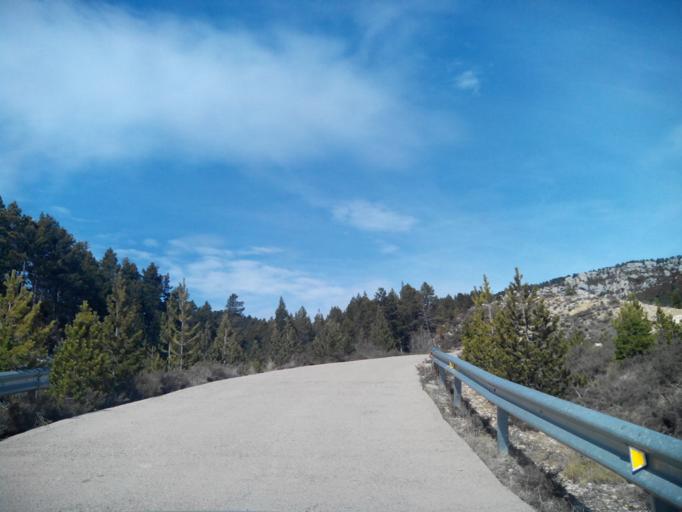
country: ES
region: Catalonia
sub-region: Provincia de Barcelona
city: Vallcebre
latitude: 42.1995
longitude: 1.7867
